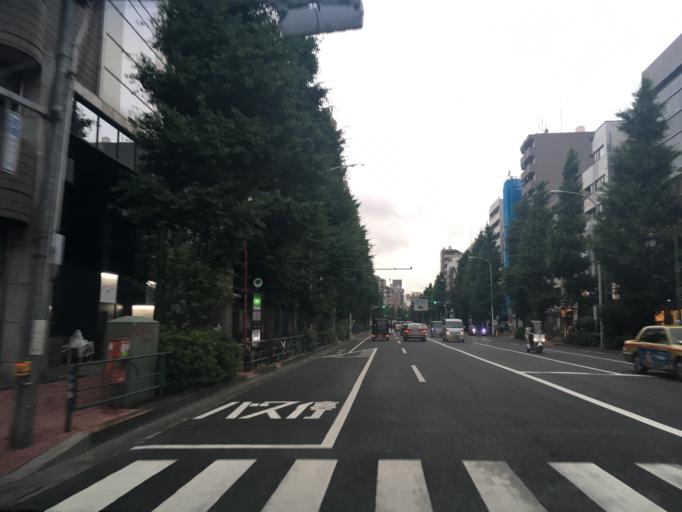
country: JP
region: Tokyo
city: Tokyo
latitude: 35.6974
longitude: 139.6661
